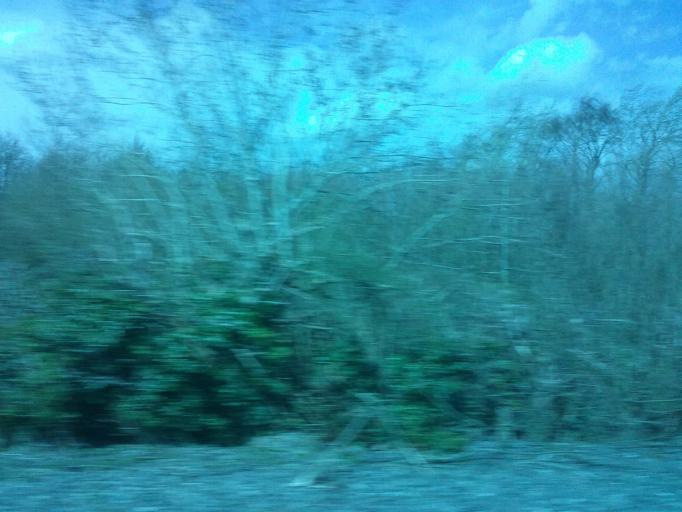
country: IE
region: Leinster
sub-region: Kildare
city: Johnstown
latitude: 53.2664
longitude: -6.6302
